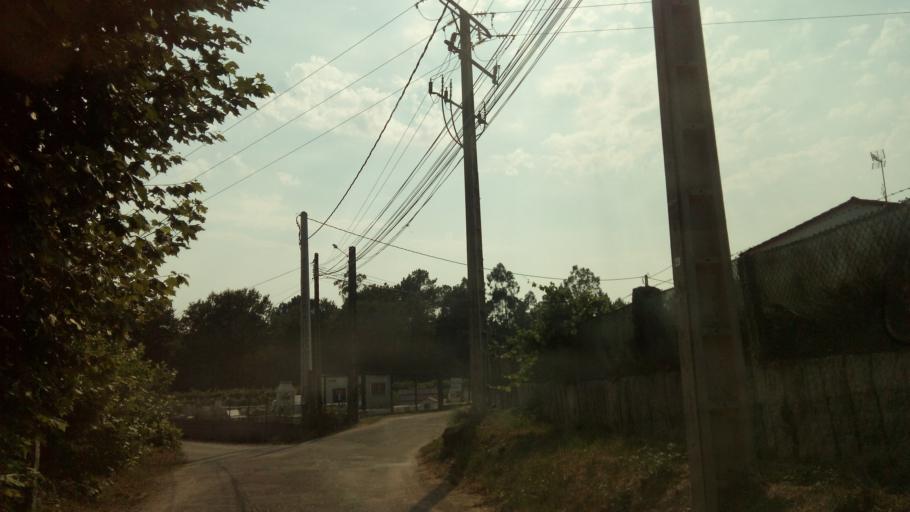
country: ES
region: Galicia
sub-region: Provincia de Pontevedra
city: Ponteareas
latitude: 42.1859
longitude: -8.5075
